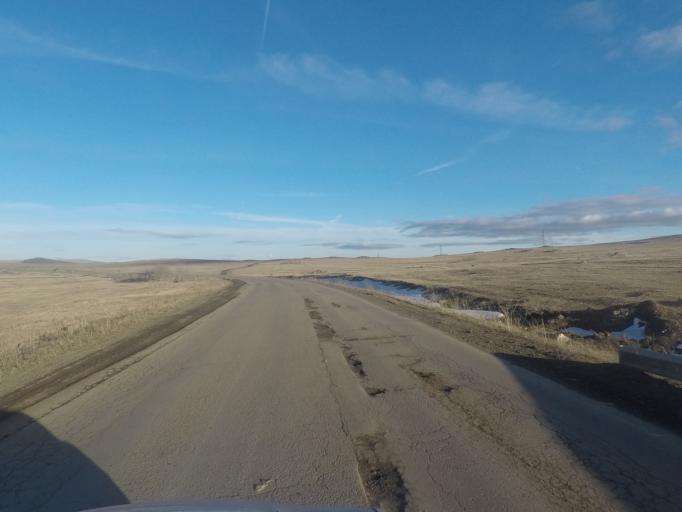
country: GE
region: Kvemo Kartli
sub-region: Tsalka
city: Tsalka
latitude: 41.5979
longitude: 44.0229
